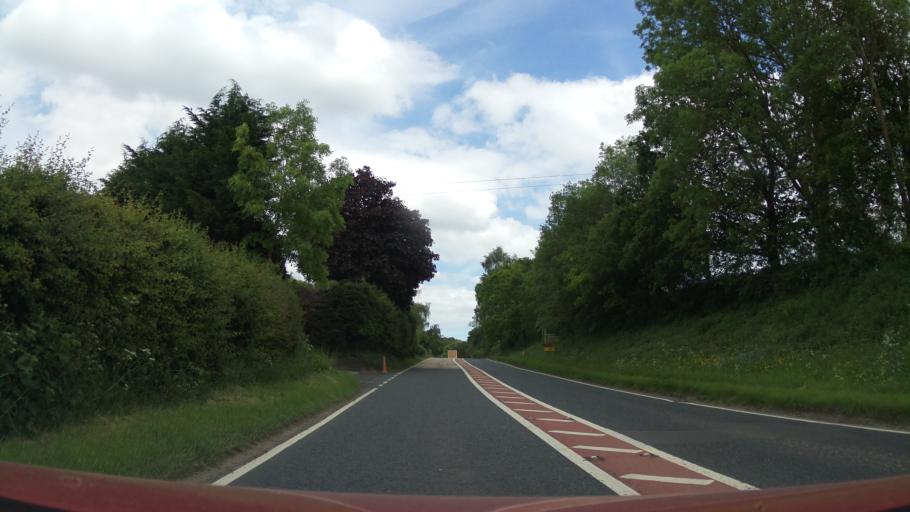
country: GB
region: England
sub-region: Worcestershire
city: Great Malvern
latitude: 52.1358
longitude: -2.3684
